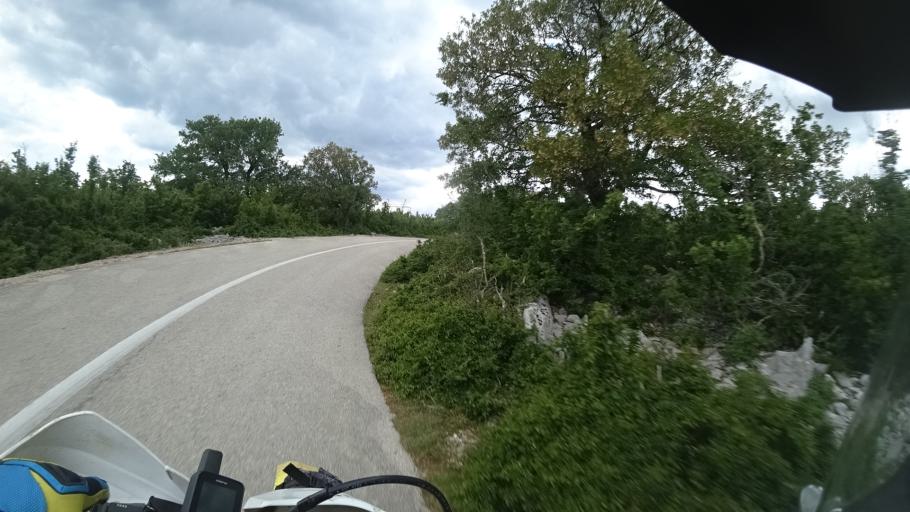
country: HR
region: Zadarska
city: Gracac
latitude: 44.1986
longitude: 15.8719
